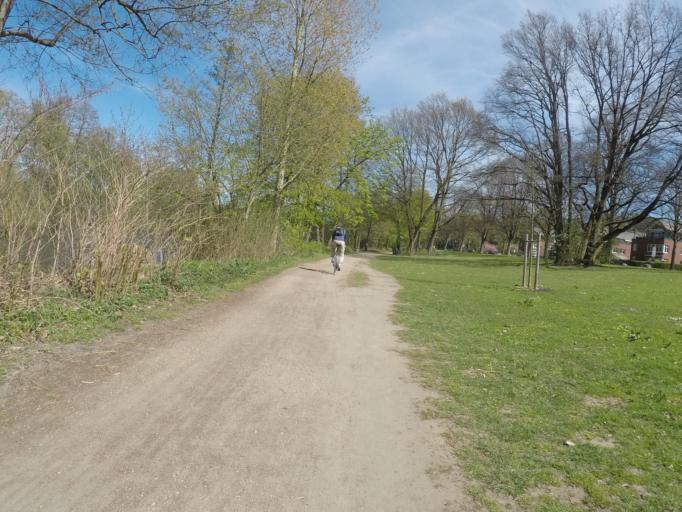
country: DE
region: Hamburg
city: Ohlsdorf
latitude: 53.6184
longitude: 10.0244
